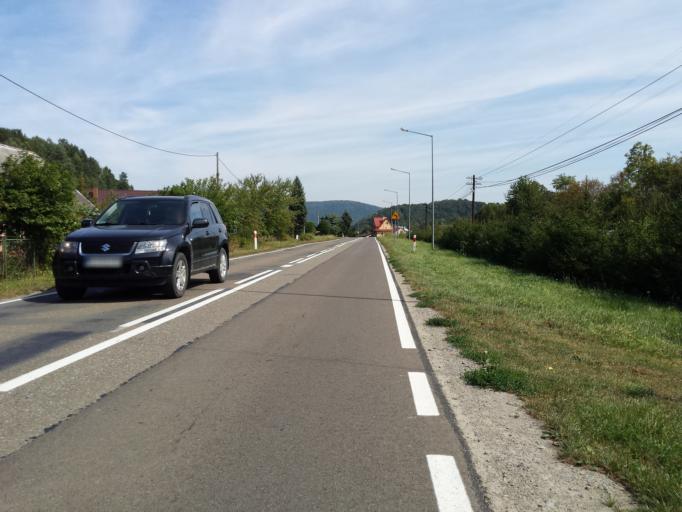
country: PL
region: Subcarpathian Voivodeship
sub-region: Powiat leski
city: Lesko
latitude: 49.4173
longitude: 22.3172
